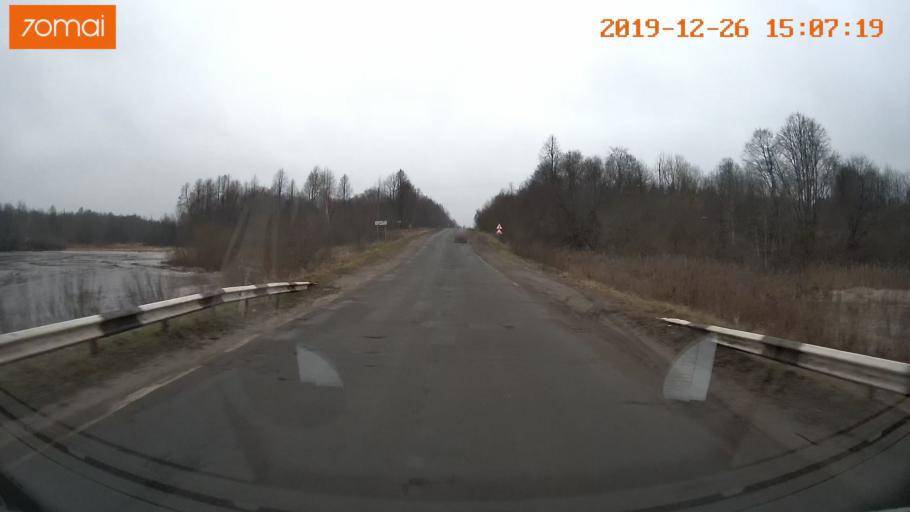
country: RU
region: Jaroslavl
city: Rybinsk
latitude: 58.1710
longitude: 38.8407
